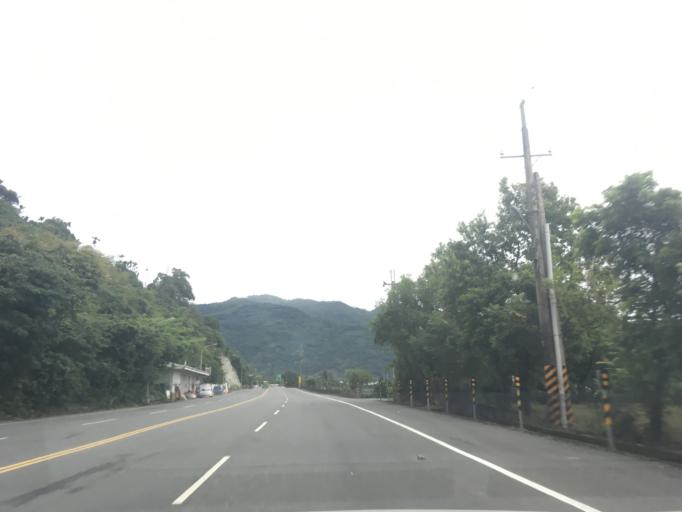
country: TW
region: Taiwan
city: Taitung City
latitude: 22.7522
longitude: 121.0540
